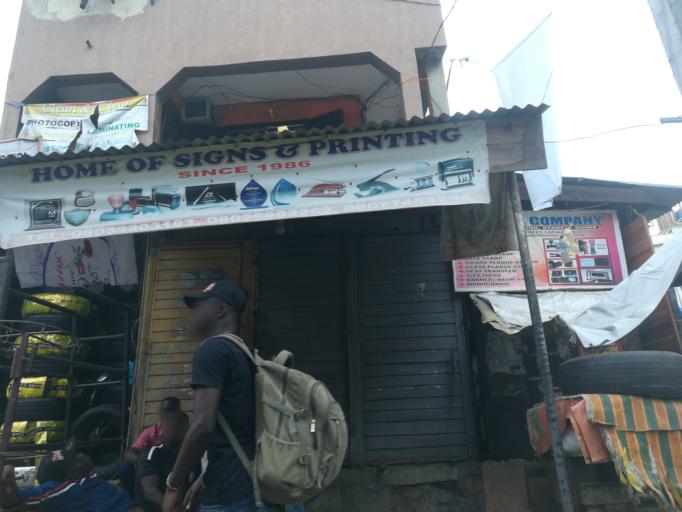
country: NG
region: Lagos
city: Lagos
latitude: 6.4507
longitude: 3.4031
